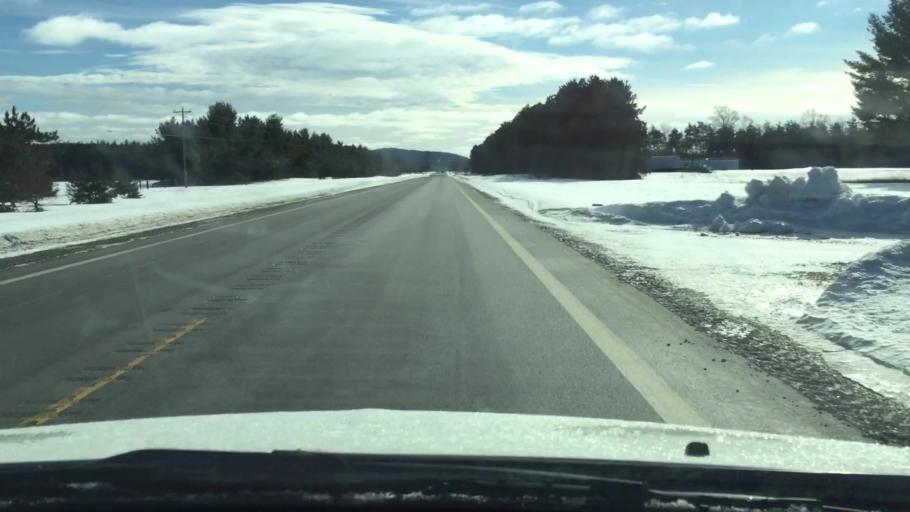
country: US
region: Michigan
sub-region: Antrim County
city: Mancelona
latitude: 44.9268
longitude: -85.0509
